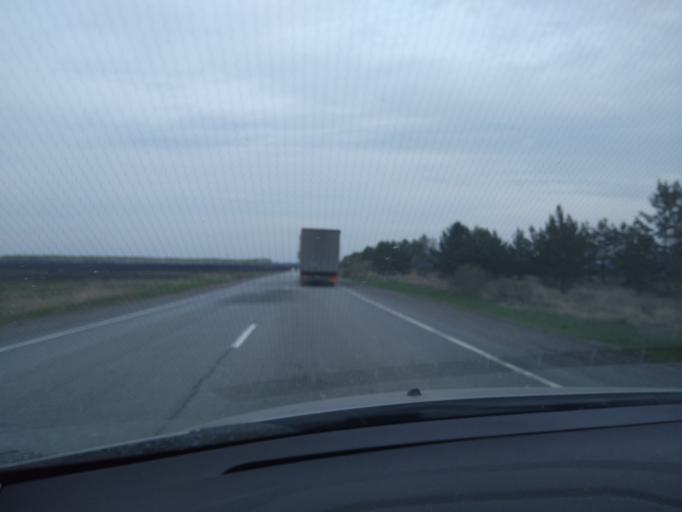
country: RU
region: Sverdlovsk
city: Yelanskiy
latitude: 56.7694
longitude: 62.4368
